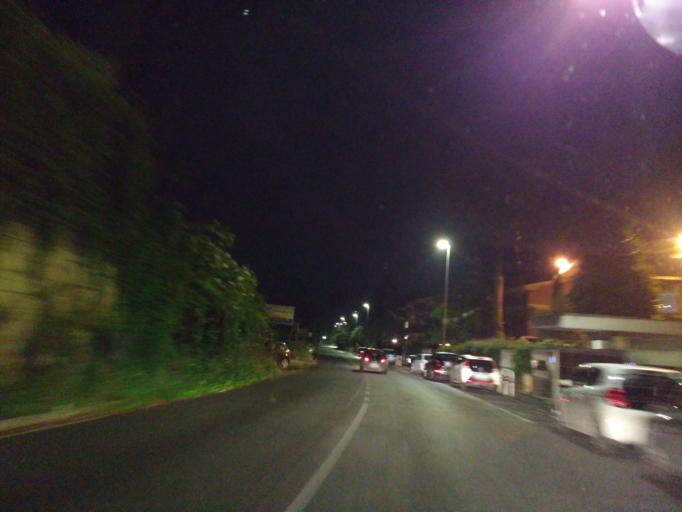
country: IT
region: Latium
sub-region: Citta metropolitana di Roma Capitale
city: Vitinia
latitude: 41.7860
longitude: 12.4292
